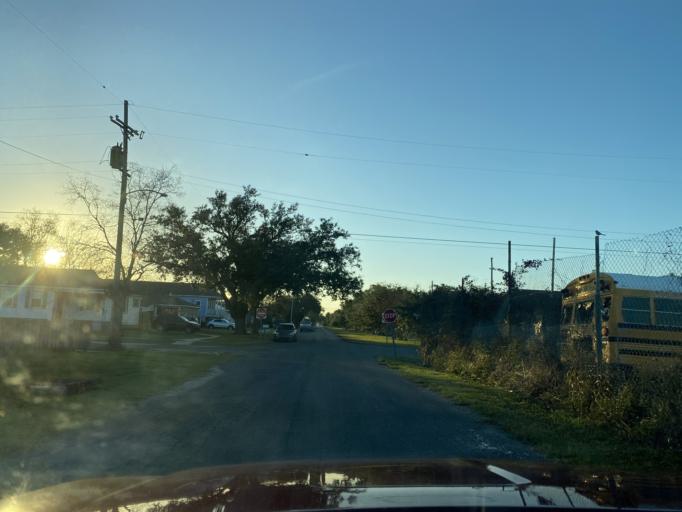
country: US
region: Louisiana
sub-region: Orleans Parish
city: New Orleans
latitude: 30.0227
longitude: -90.0481
